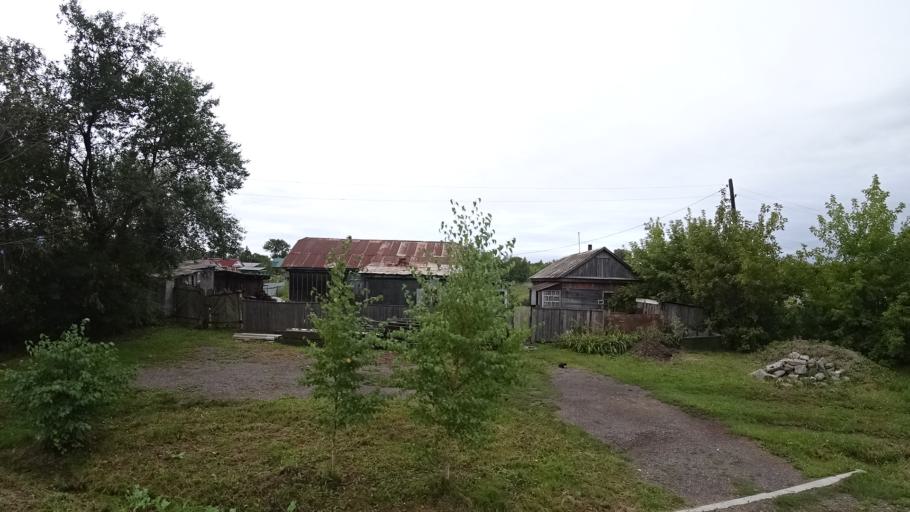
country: RU
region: Primorskiy
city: Chernigovka
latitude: 44.3344
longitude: 132.5677
